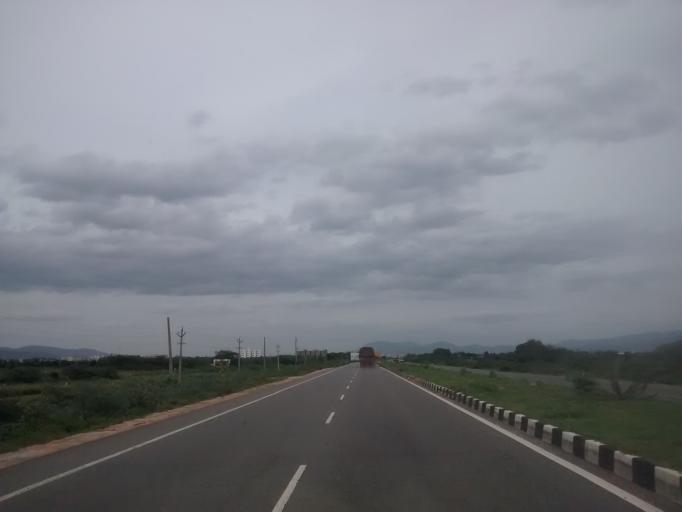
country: IN
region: Andhra Pradesh
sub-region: Chittoor
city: Tirupati
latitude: 13.6041
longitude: 79.3815
